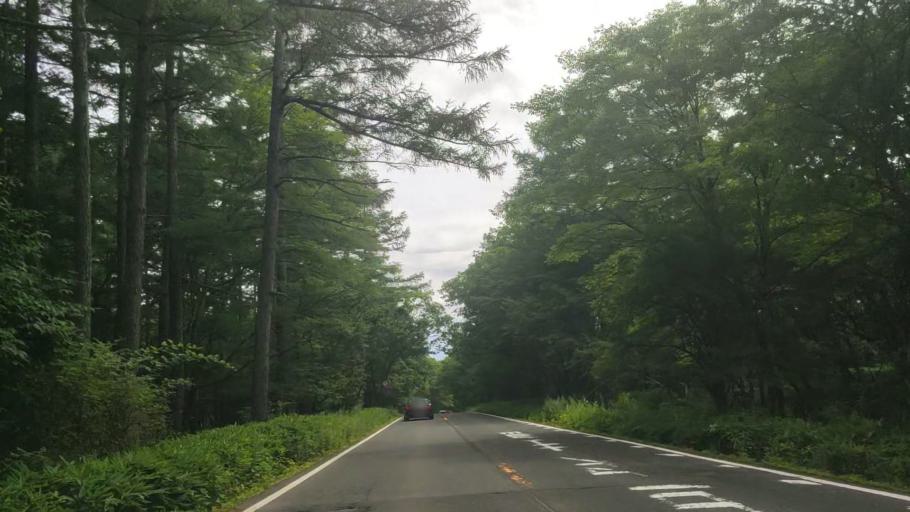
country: JP
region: Tochigi
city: Nikko
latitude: 36.7678
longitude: 139.4529
